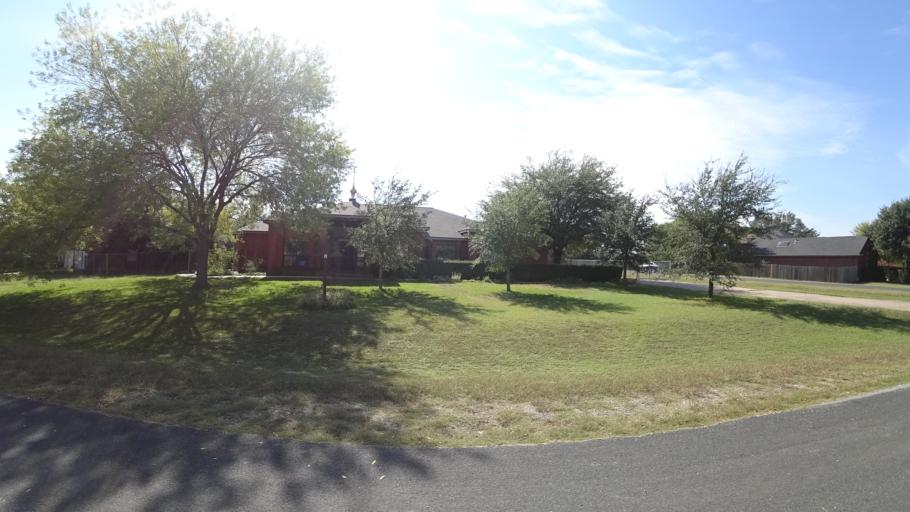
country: US
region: Texas
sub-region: Travis County
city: Pflugerville
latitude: 30.4148
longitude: -97.6290
